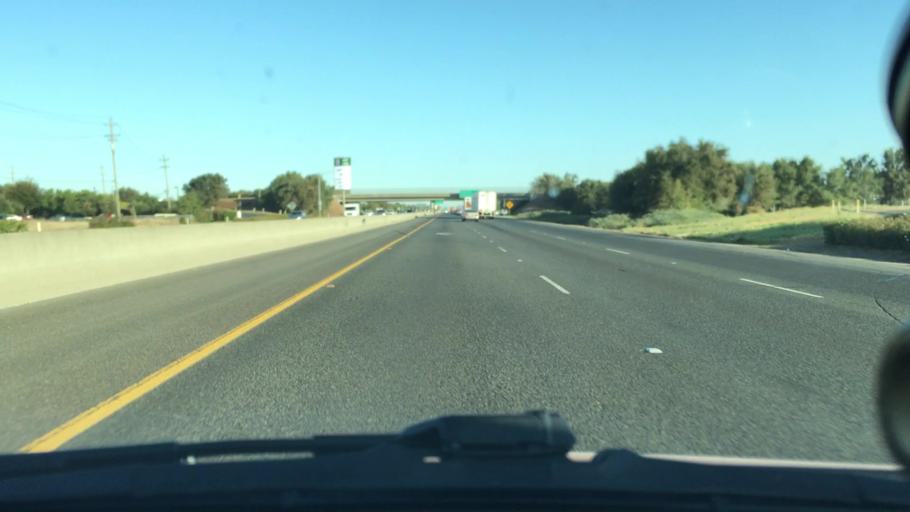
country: US
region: California
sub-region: Sacramento County
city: Elk Grove
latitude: 38.4210
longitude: -121.3941
